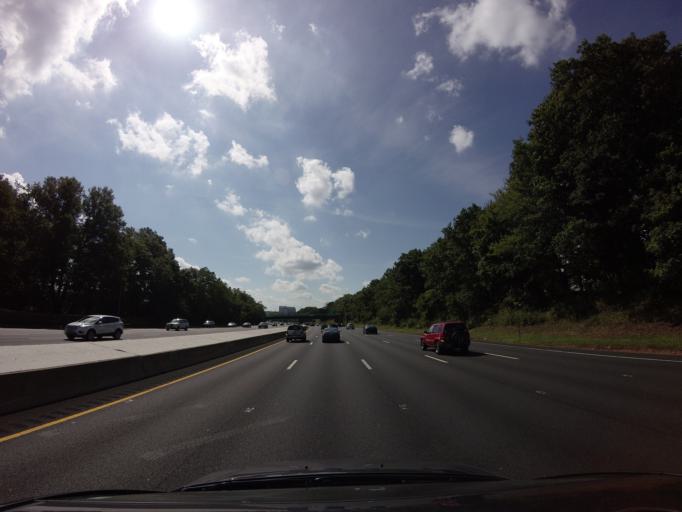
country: US
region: New Jersey
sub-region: Middlesex County
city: Iselin
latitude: 40.5753
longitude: -74.3308
